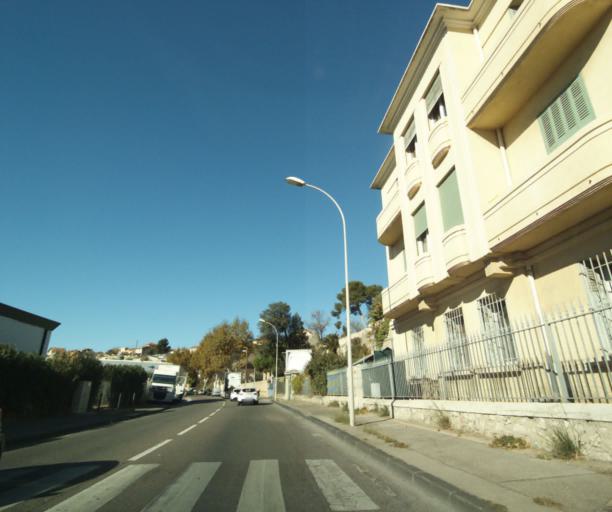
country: FR
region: Provence-Alpes-Cote d'Azur
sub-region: Departement des Bouches-du-Rhone
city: Marseille 16
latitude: 43.3539
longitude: 5.3362
